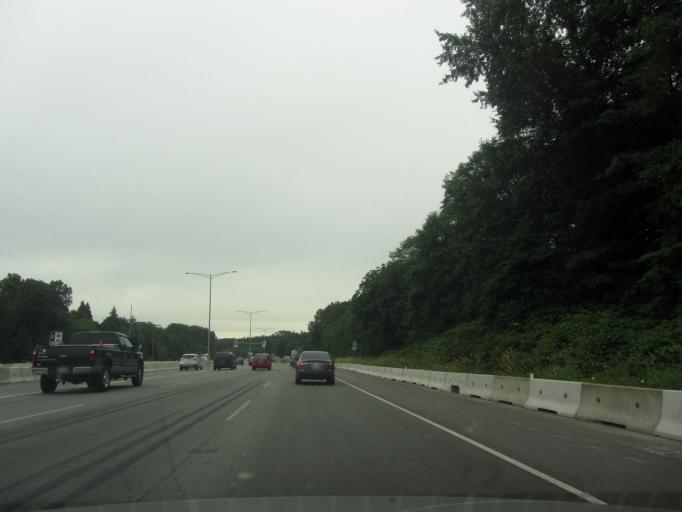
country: CA
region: British Columbia
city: Burnaby
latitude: 49.2577
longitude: -122.9892
